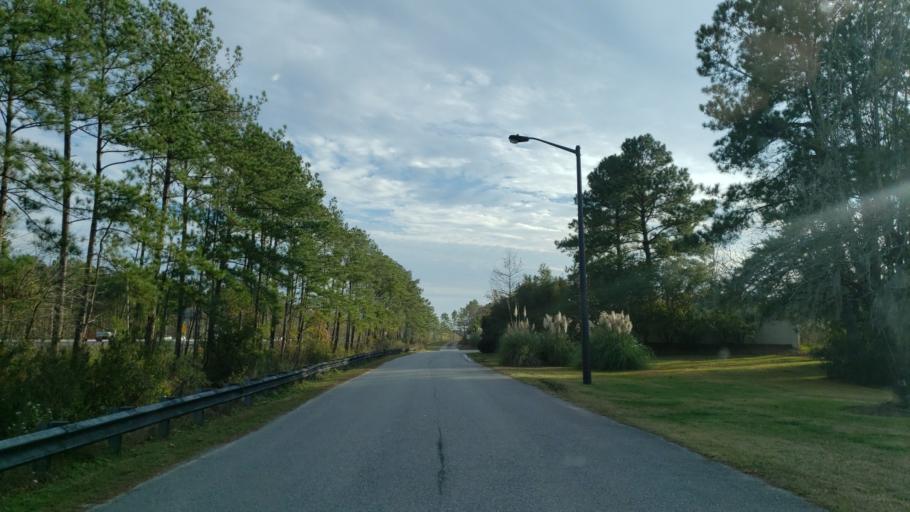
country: US
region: Georgia
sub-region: Chatham County
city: Pooler
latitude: 32.1091
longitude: -81.2385
